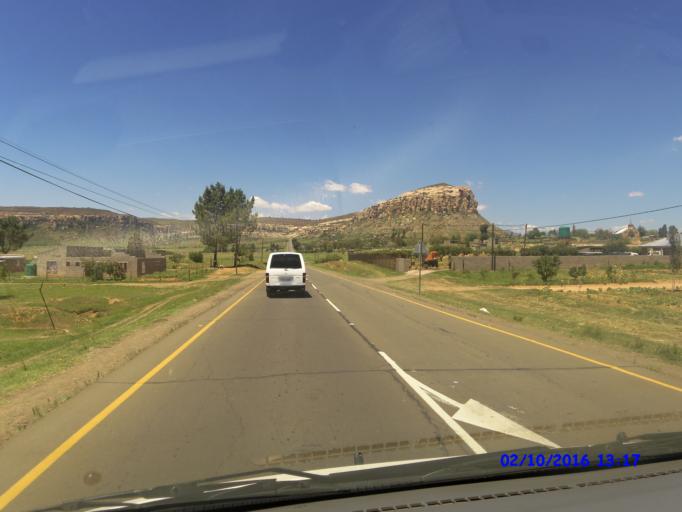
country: LS
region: Maseru
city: Nako
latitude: -29.4234
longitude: 27.6761
